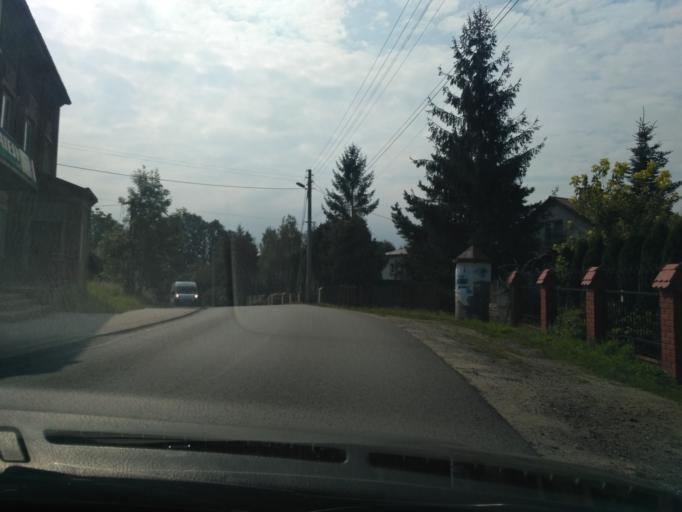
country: PL
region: Subcarpathian Voivodeship
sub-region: Powiat rzeszowski
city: Kielanowka
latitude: 50.0055
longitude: 21.9093
